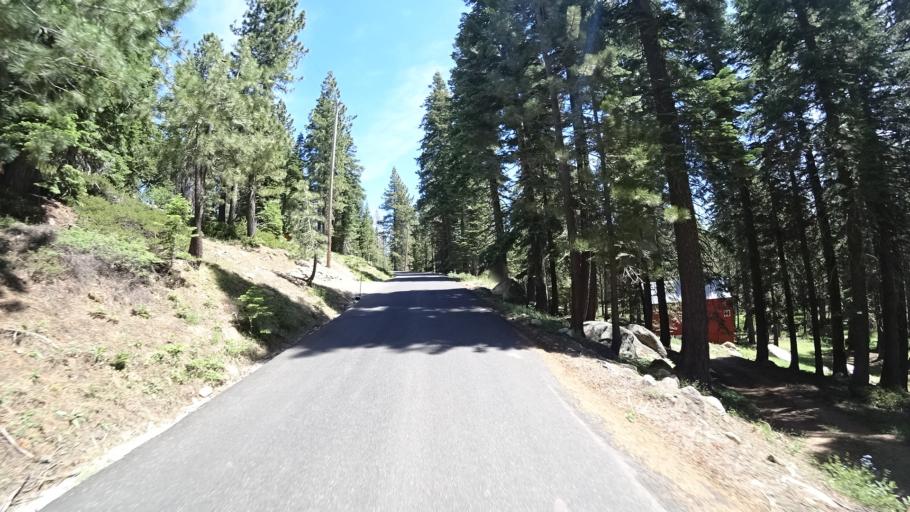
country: US
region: California
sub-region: Calaveras County
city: Arnold
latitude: 38.4239
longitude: -120.0941
